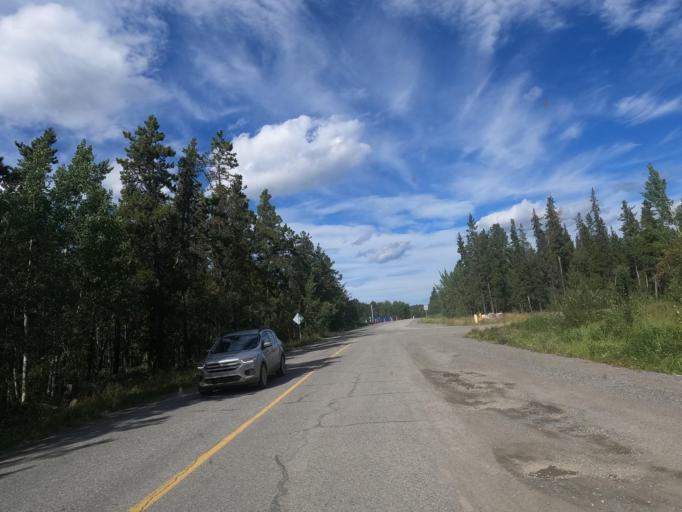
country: CA
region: Yukon
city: Whitehorse
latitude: 60.6972
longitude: -135.0407
